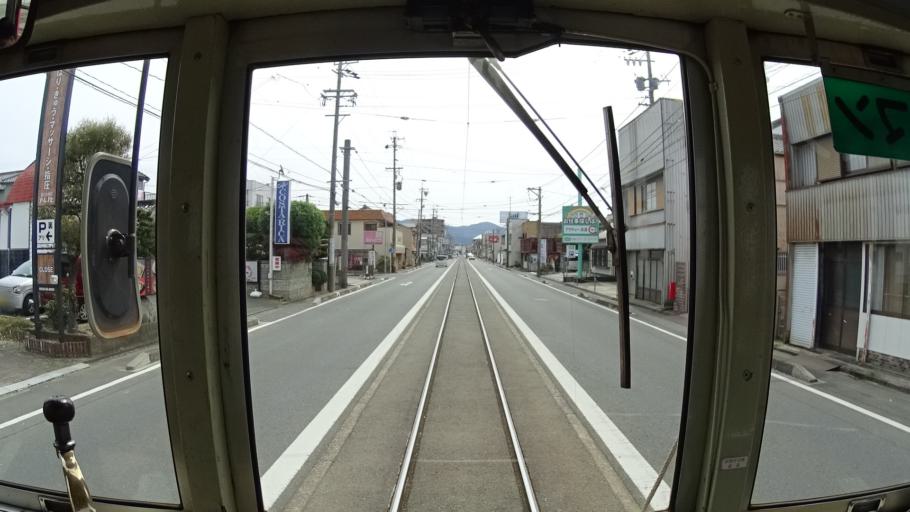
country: JP
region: Aichi
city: Toyohashi
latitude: 34.7646
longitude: 137.4197
